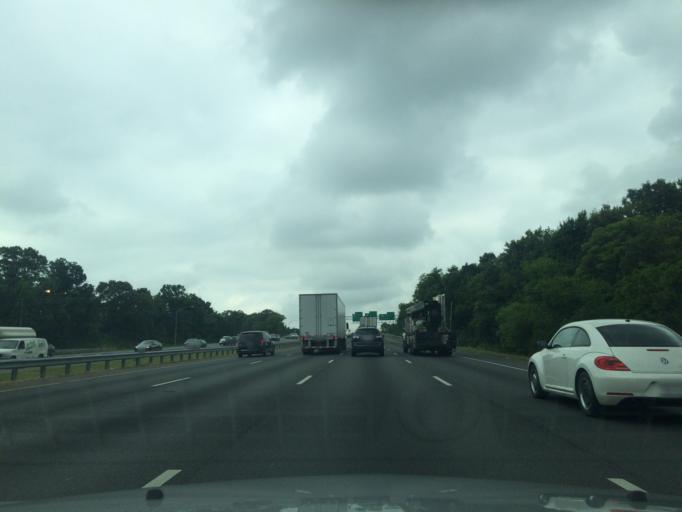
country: US
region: Maryland
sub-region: Prince George's County
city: Forestville
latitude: 38.8448
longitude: -76.8635
